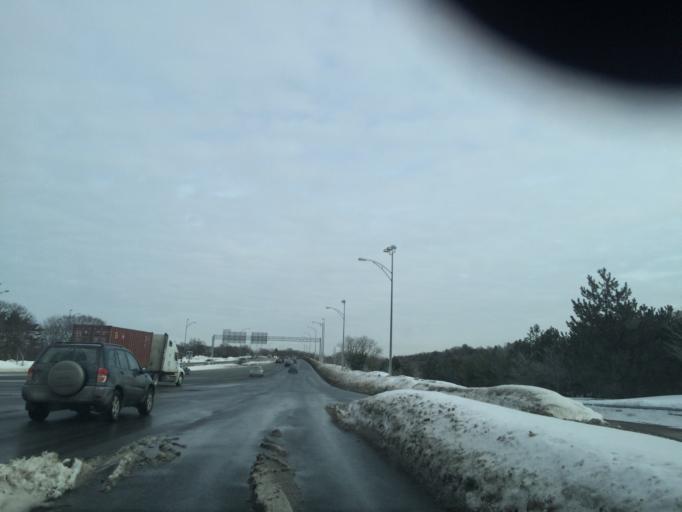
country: US
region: Massachusetts
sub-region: Middlesex County
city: Waltham
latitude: 42.3387
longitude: -71.2645
